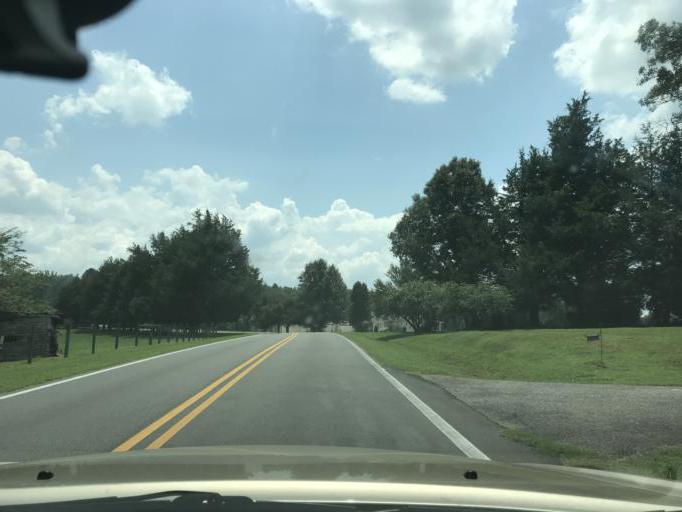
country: US
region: Georgia
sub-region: Forsyth County
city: Cumming
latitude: 34.2621
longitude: -84.2207
